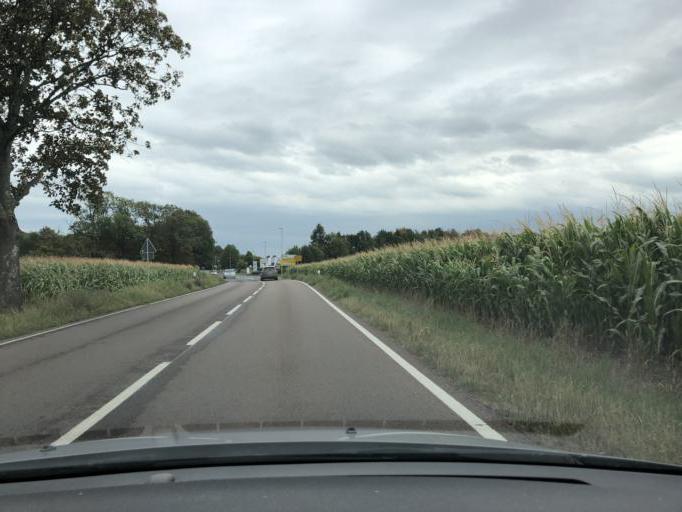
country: DE
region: Saxony-Anhalt
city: Koethen
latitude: 51.7565
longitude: 11.9435
